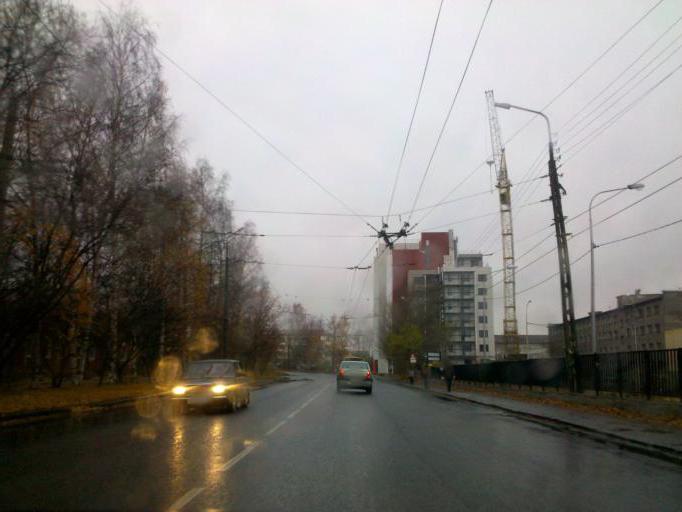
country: RU
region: Republic of Karelia
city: Petrozavodsk
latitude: 61.7995
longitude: 34.3244
